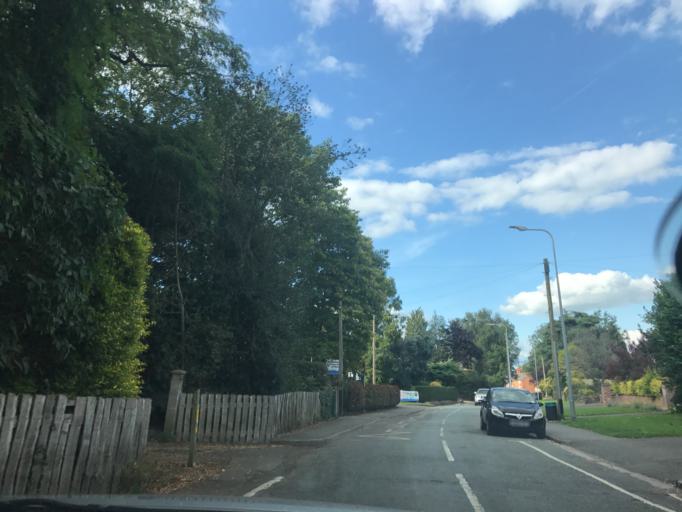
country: GB
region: England
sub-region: Cheshire East
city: Nantwich
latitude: 53.0652
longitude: -2.5315
